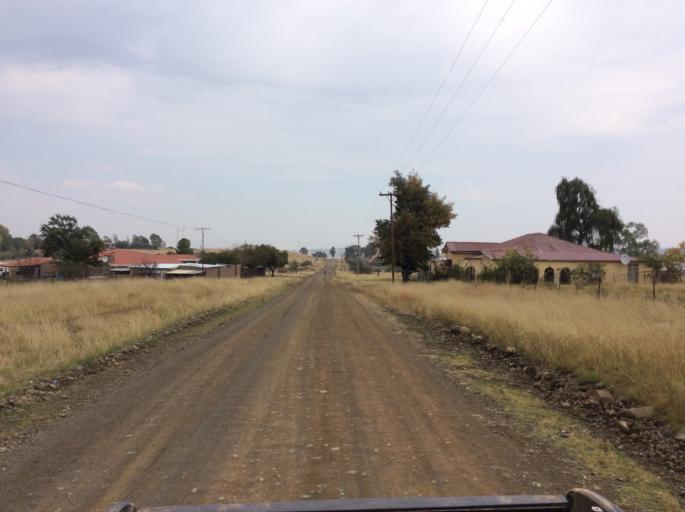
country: LS
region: Mafeteng
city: Mafeteng
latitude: -29.9857
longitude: 27.0127
